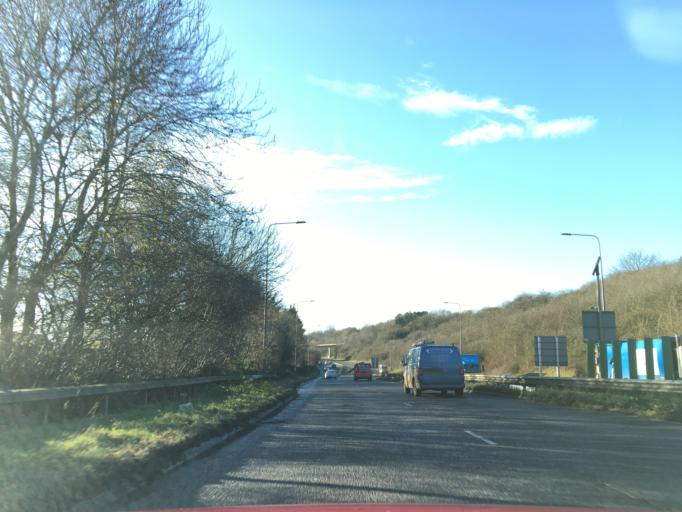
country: GB
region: England
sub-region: South Gloucestershire
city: Kingswood
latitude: 51.4530
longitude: -2.4875
